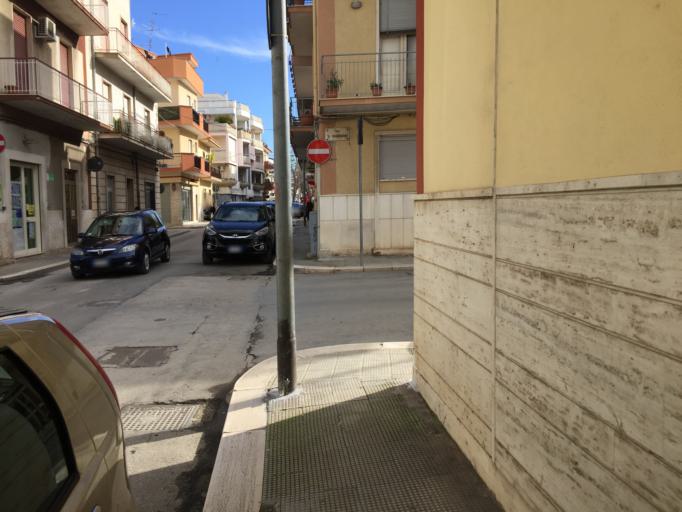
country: IT
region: Apulia
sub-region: Provincia di Barletta - Andria - Trani
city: Andria
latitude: 41.2252
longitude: 16.3058
